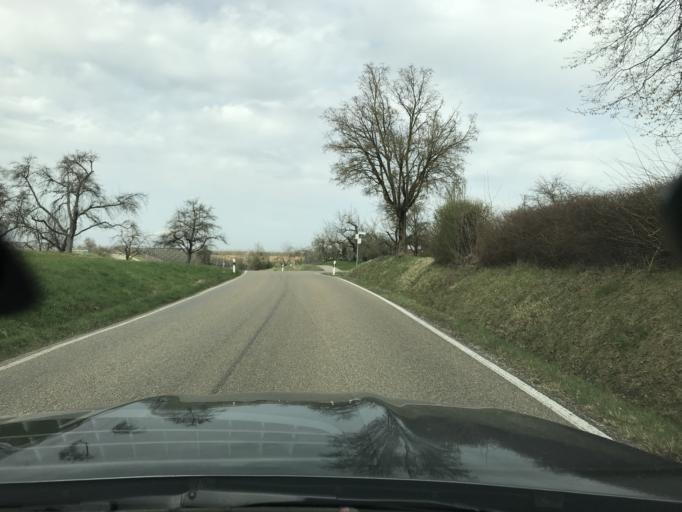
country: DE
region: Baden-Wuerttemberg
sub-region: Regierungsbezirk Stuttgart
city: Leutenbach
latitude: 48.9051
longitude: 9.3790
